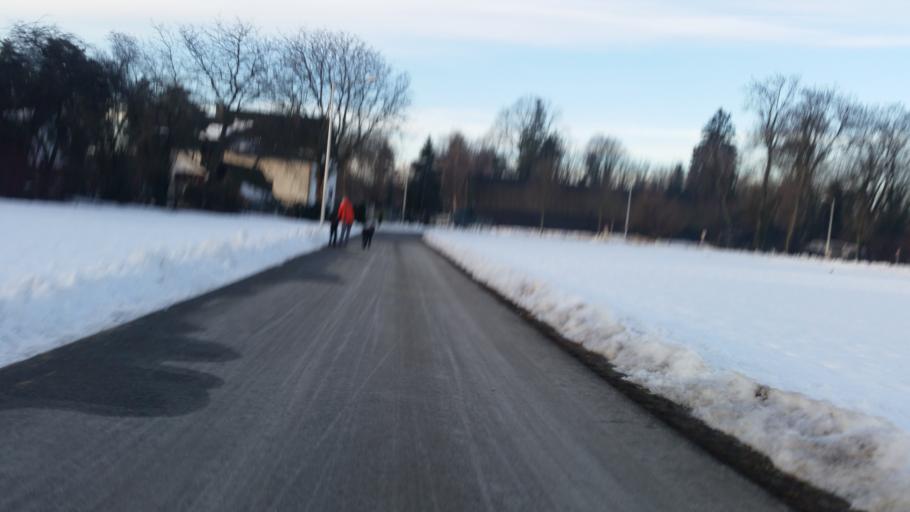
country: AT
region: Vorarlberg
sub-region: Politischer Bezirk Bregenz
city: Hard
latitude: 47.5004
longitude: 9.7063
